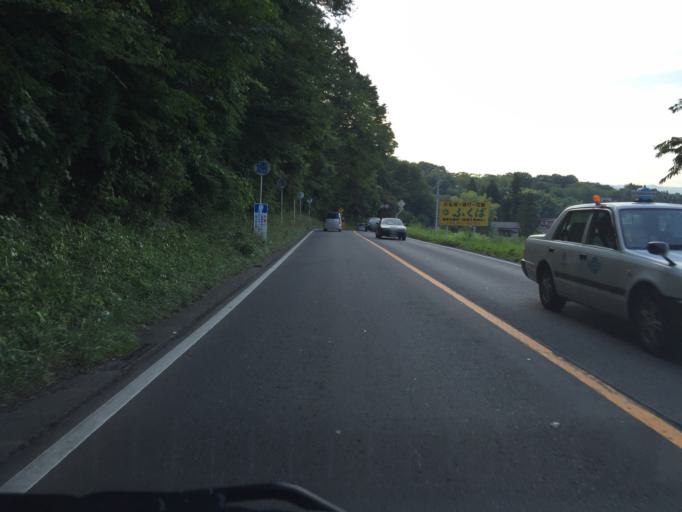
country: JP
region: Fukushima
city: Fukushima-shi
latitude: 37.7144
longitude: 140.4645
